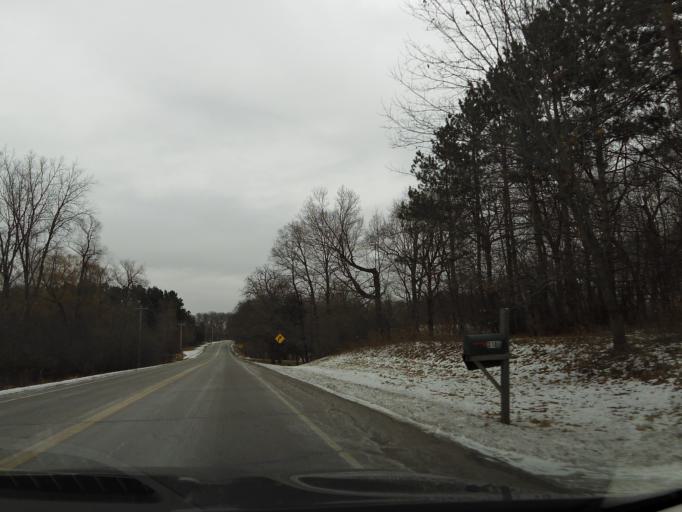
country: US
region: Minnesota
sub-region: Hennepin County
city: Orono
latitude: 44.9974
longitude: -93.6039
